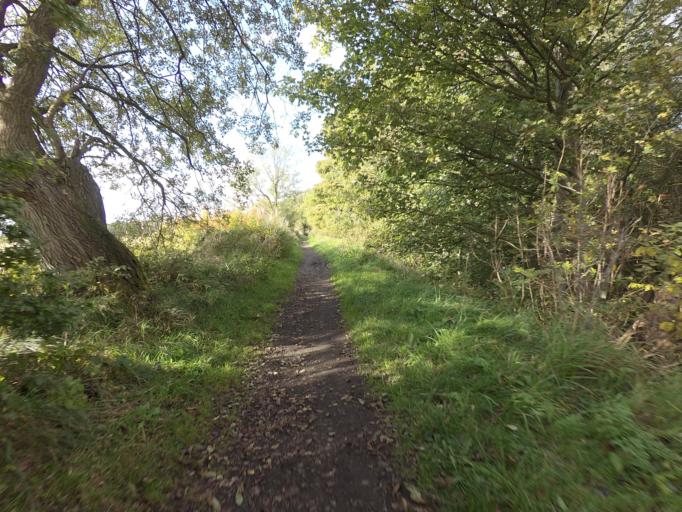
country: GB
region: Scotland
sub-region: West Lothian
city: East Calder
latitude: 55.9045
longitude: -3.4696
